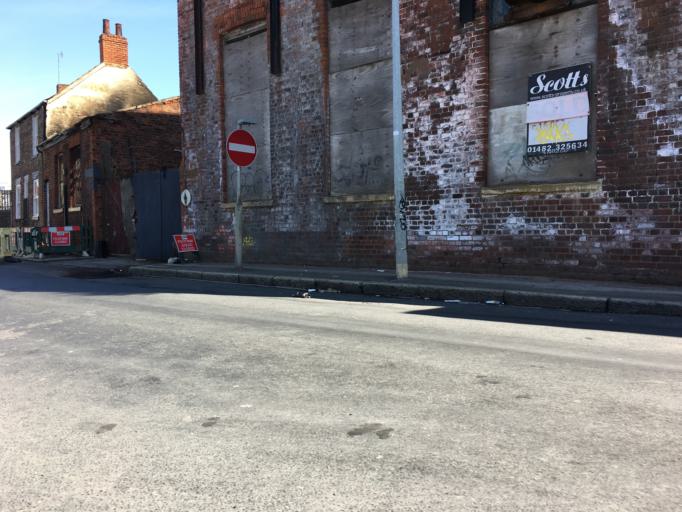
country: GB
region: England
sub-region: City of Kingston upon Hull
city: Hull
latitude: 53.7525
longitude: -0.3328
